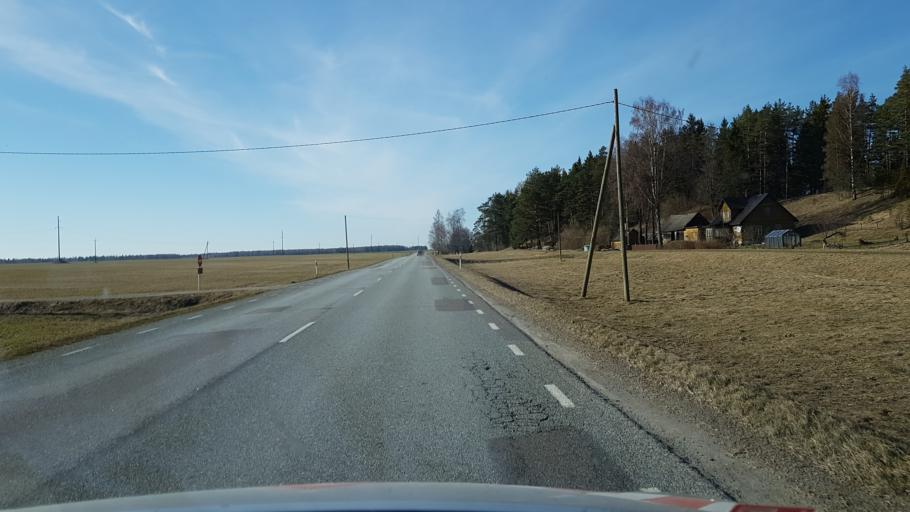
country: EE
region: Laeaene-Virumaa
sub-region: Vinni vald
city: Vinni
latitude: 59.1927
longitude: 26.5690
